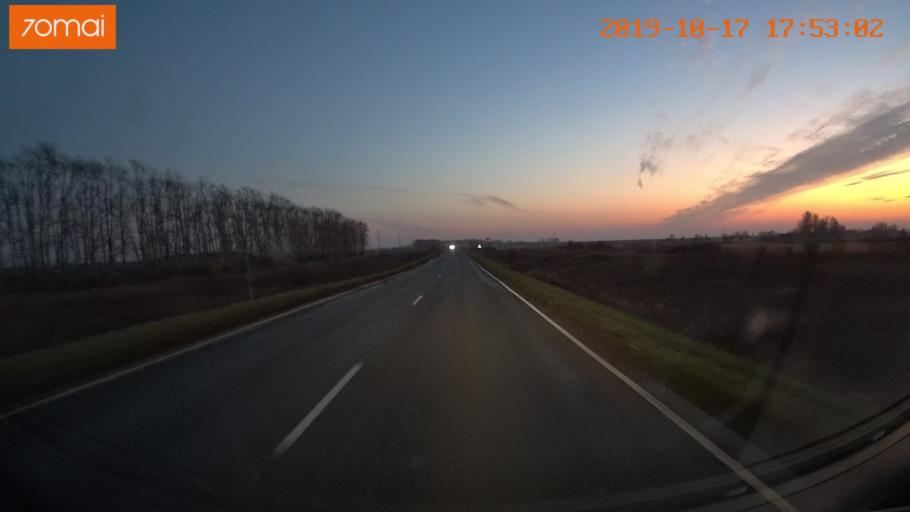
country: RU
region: Tula
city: Kurkino
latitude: 53.6256
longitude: 38.6810
